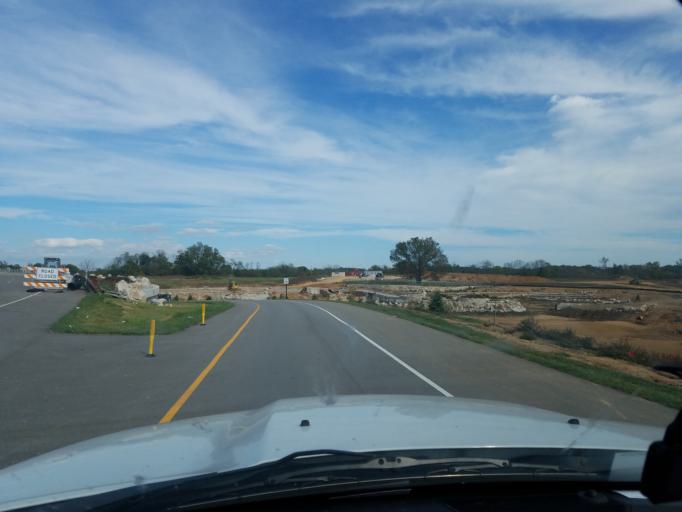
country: US
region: Kentucky
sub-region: Jefferson County
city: Prospect
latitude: 38.3552
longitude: -85.6665
